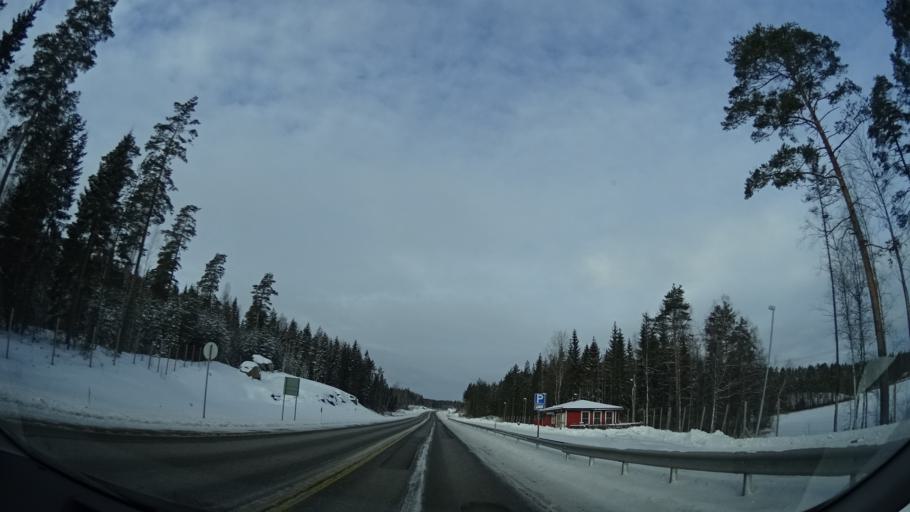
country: FI
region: Uusimaa
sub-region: Helsinki
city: Karkkila
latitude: 60.5908
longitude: 24.1092
